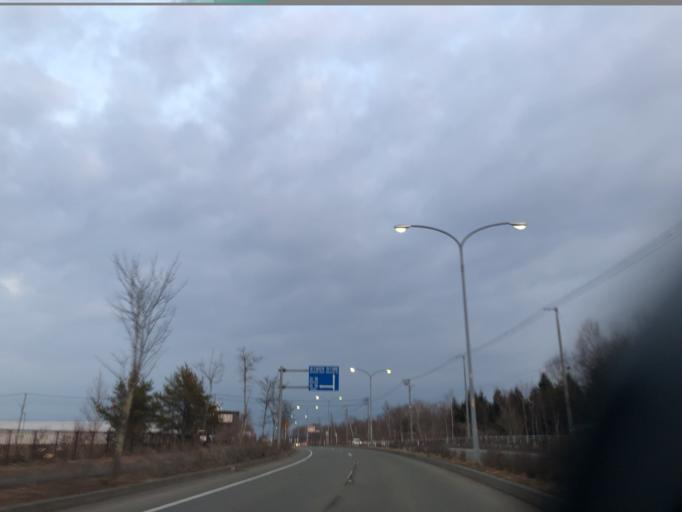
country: JP
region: Hokkaido
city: Chitose
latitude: 42.8216
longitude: 141.6727
